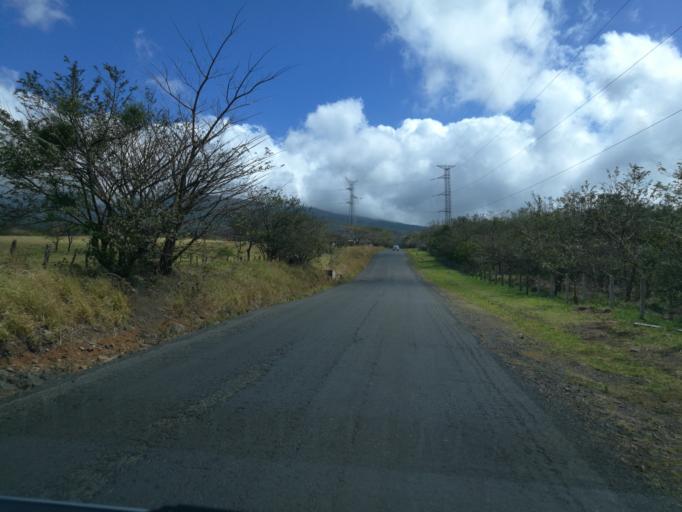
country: CR
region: Guanacaste
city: Liberia
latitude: 10.7580
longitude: -85.3621
